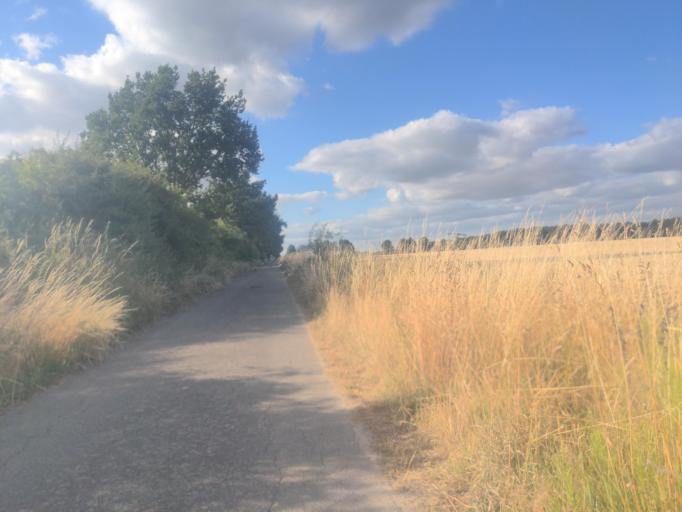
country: DE
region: Lower Saxony
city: Tosterglope
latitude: 53.2128
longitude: 10.8202
